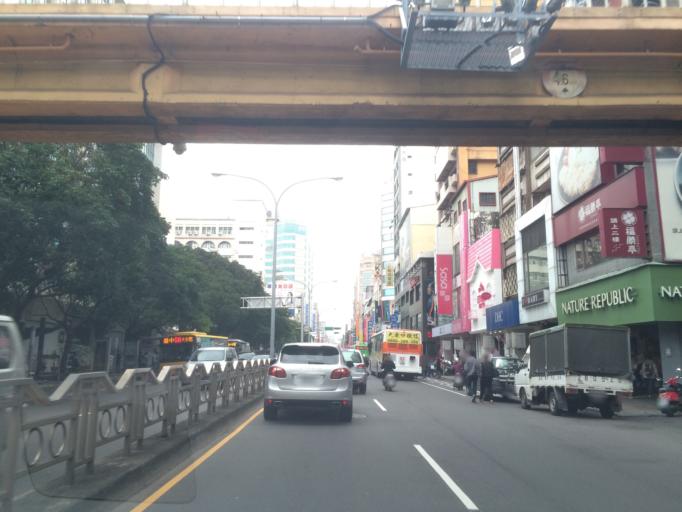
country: TW
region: Taiwan
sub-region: Taichung City
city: Taichung
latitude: 24.1489
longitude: 120.6838
